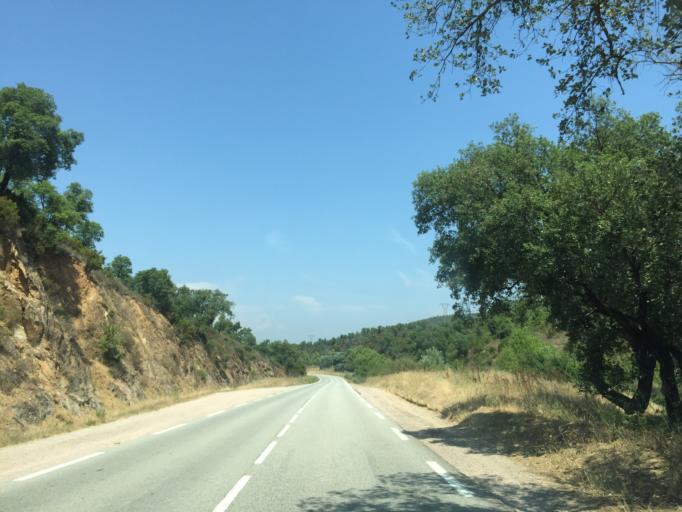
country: FR
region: Provence-Alpes-Cote d'Azur
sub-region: Departement du Var
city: Roquebrune-sur-Argens
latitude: 43.3805
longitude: 6.6748
